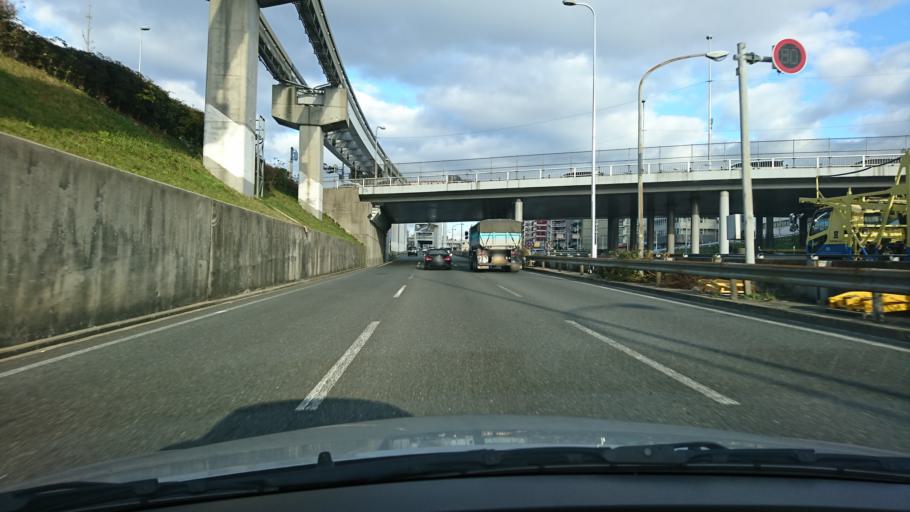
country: JP
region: Osaka
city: Toyonaka
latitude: 34.8020
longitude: 135.4709
